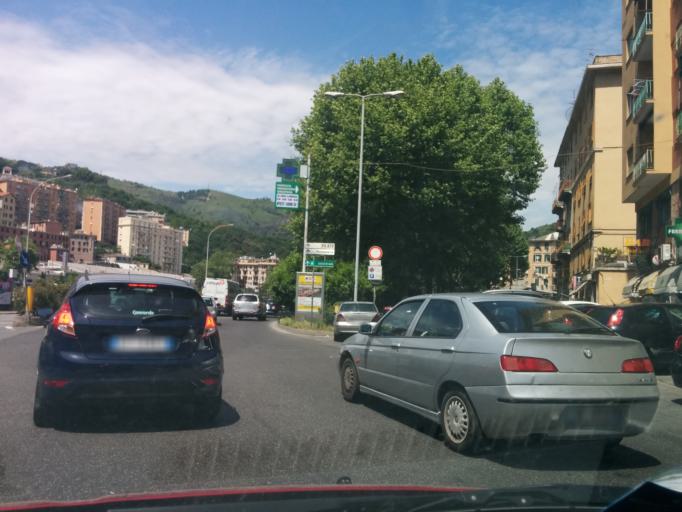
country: IT
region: Liguria
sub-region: Provincia di Genova
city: Genoa
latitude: 44.4220
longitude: 8.9484
